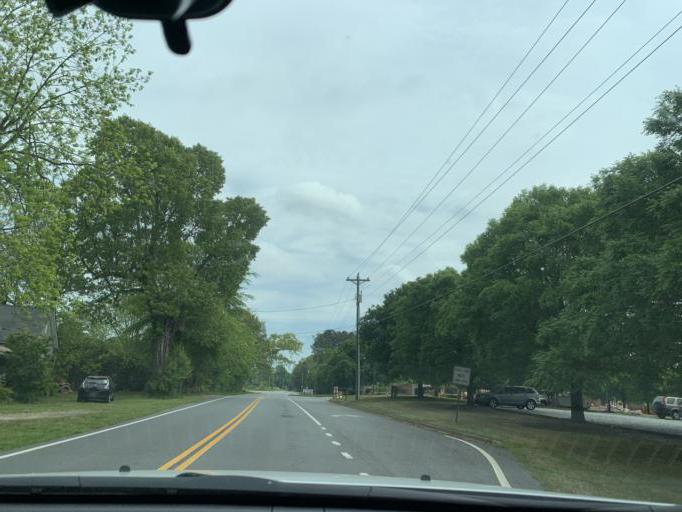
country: US
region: Georgia
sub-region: Forsyth County
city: Cumming
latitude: 34.1434
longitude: -84.2024
